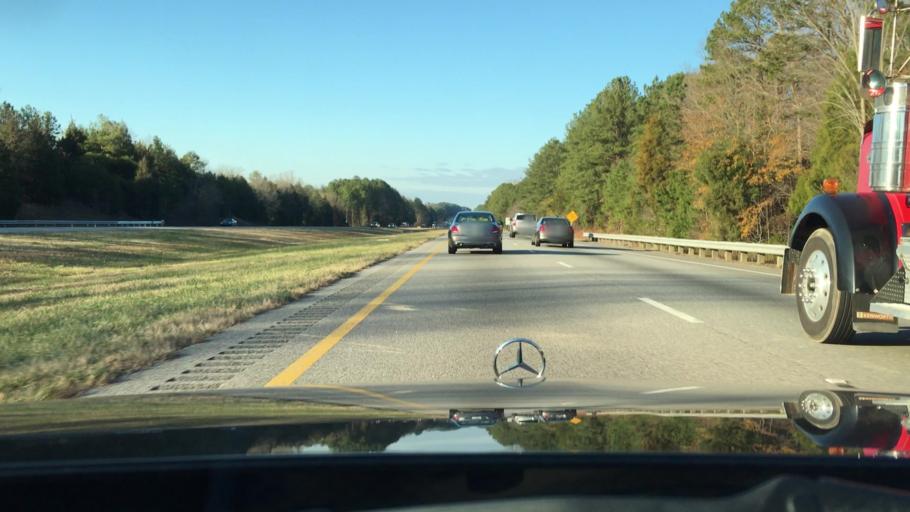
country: US
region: South Carolina
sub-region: Chester County
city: Eureka Mill
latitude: 34.7189
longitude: -81.0320
